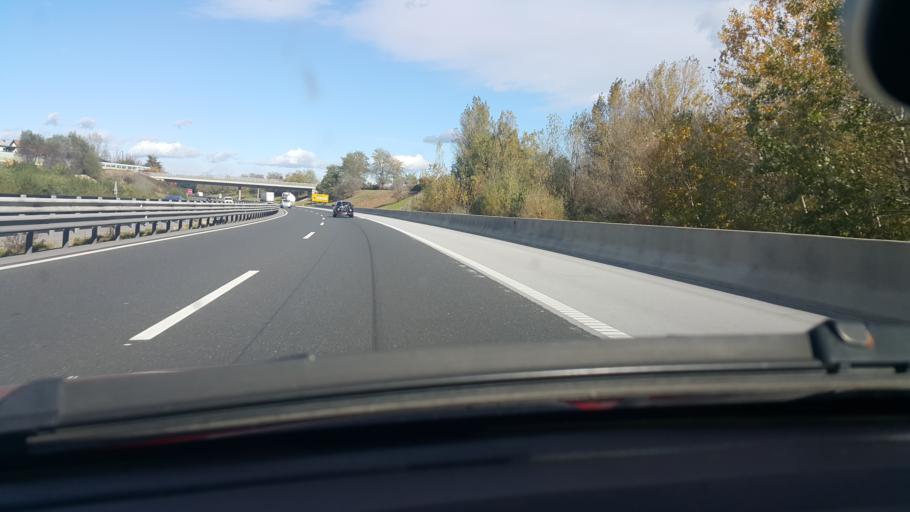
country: SI
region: Hoce-Slivnica
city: Rogoza
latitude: 46.4931
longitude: 15.6690
